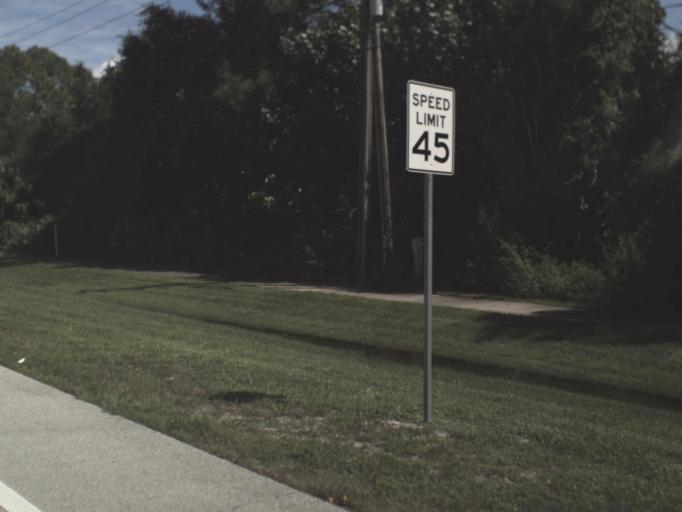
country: US
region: Florida
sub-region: Sarasota County
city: North Port
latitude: 27.0548
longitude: -82.1570
